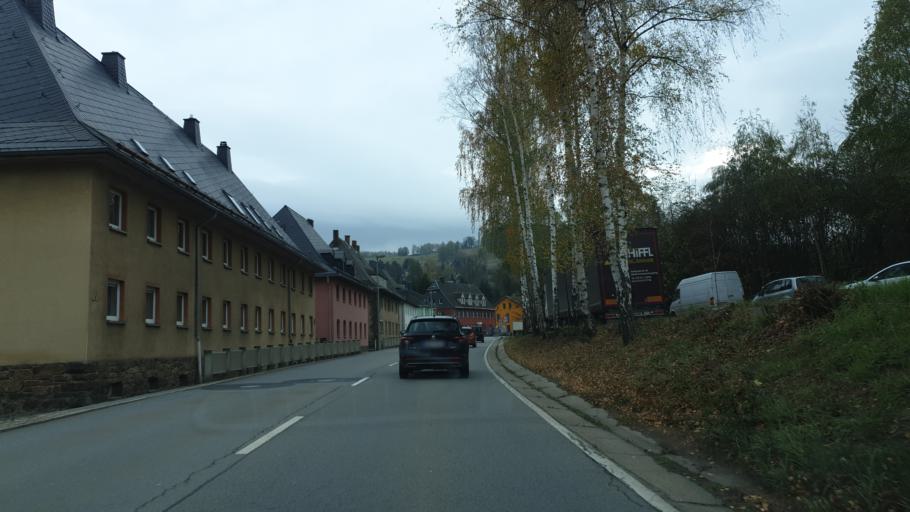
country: DE
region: Saxony
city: Schwarzenberg
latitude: 50.5210
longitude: 12.7888
